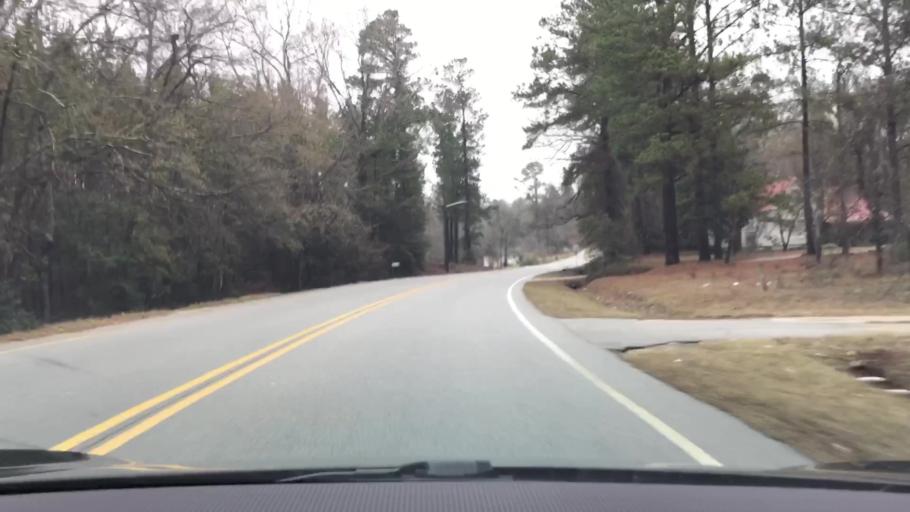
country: US
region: Georgia
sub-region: Jefferson County
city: Wrens
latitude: 33.2050
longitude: -82.4687
